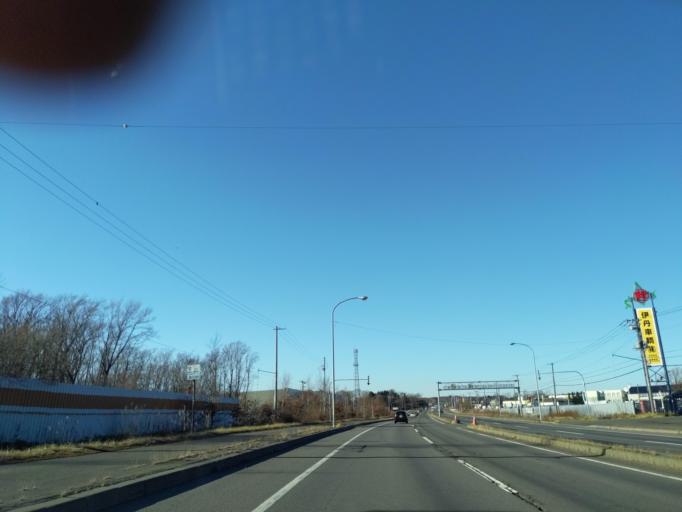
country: JP
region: Hokkaido
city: Kitahiroshima
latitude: 42.9364
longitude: 141.5134
